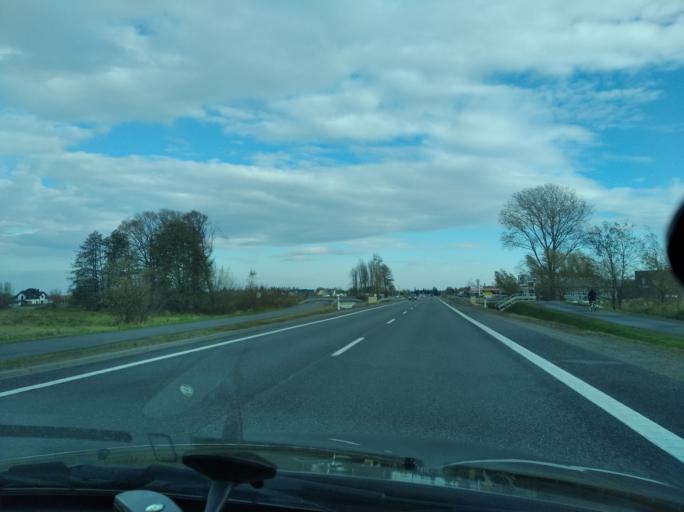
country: PL
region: Subcarpathian Voivodeship
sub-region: Powiat debicki
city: Debica
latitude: 50.0484
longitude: 21.4436
